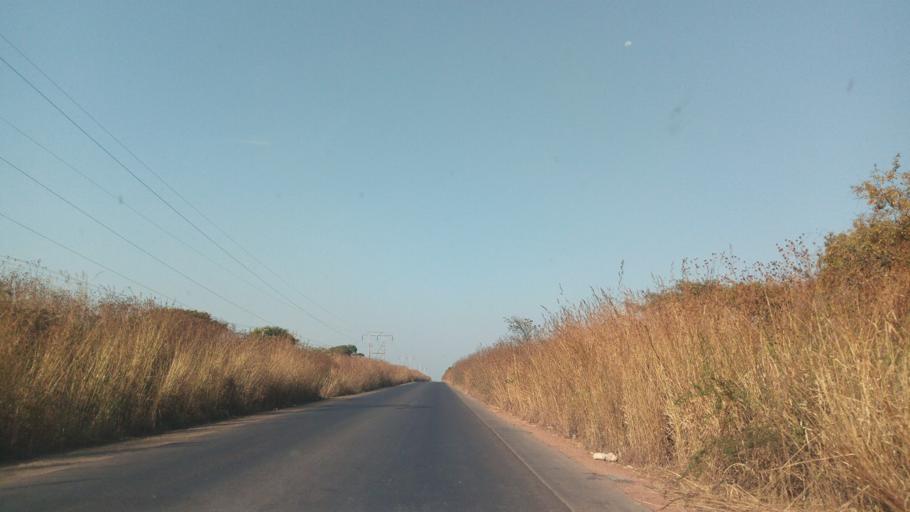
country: CD
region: Katanga
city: Likasi
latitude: -11.0015
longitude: 26.8684
